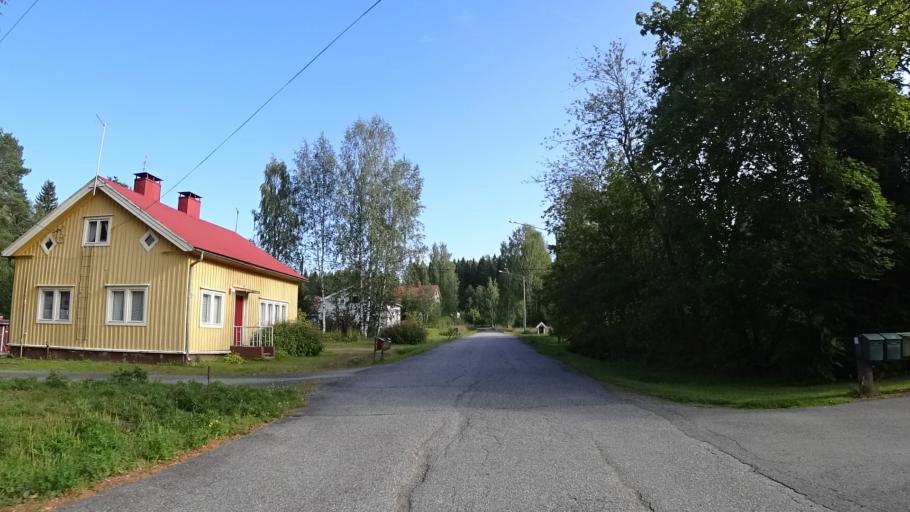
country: FI
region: North Karelia
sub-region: Joensuu
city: Eno
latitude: 62.8000
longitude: 30.1496
